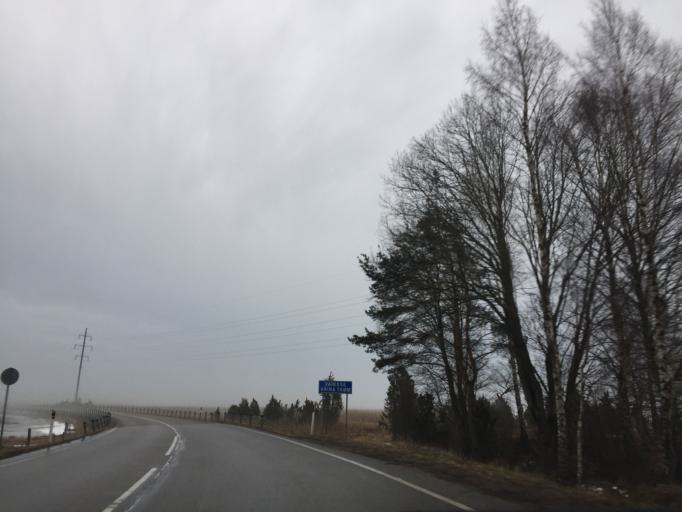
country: EE
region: Saare
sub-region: Orissaare vald
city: Orissaare
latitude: 58.5484
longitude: 23.1237
